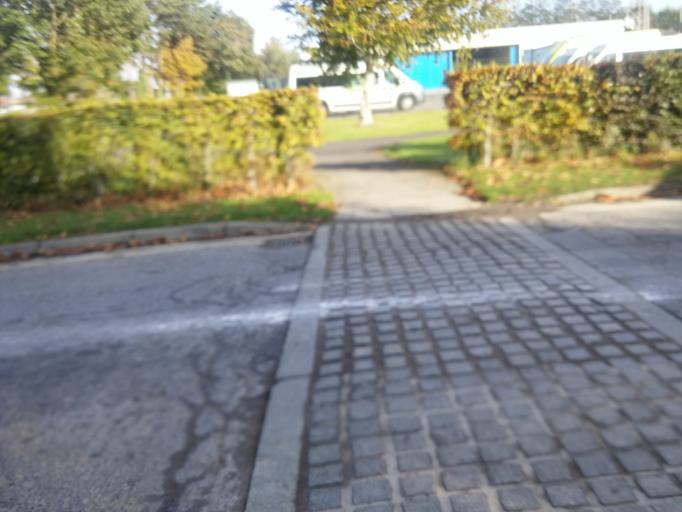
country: GB
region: Northern Ireland
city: Londonderry County Borough
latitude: 54.9876
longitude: -7.2901
